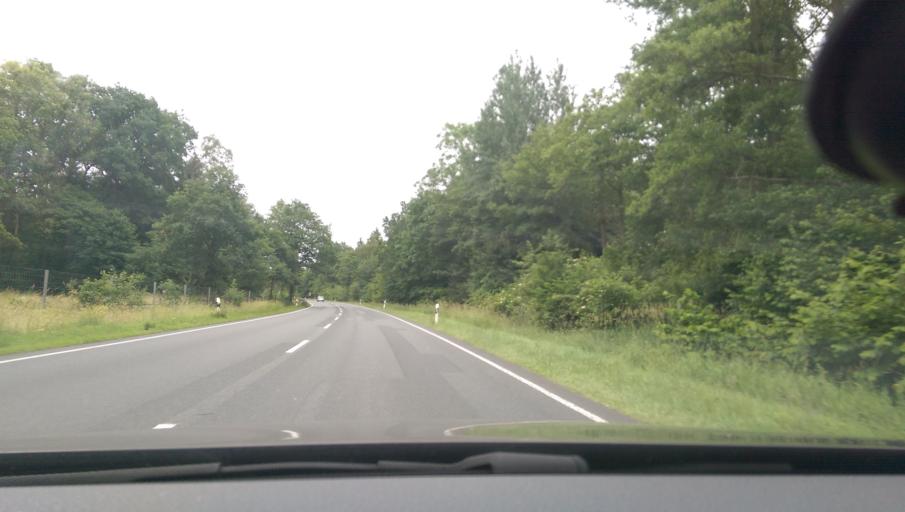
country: DE
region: Lower Saxony
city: Rotenburg
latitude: 53.1212
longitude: 9.3789
